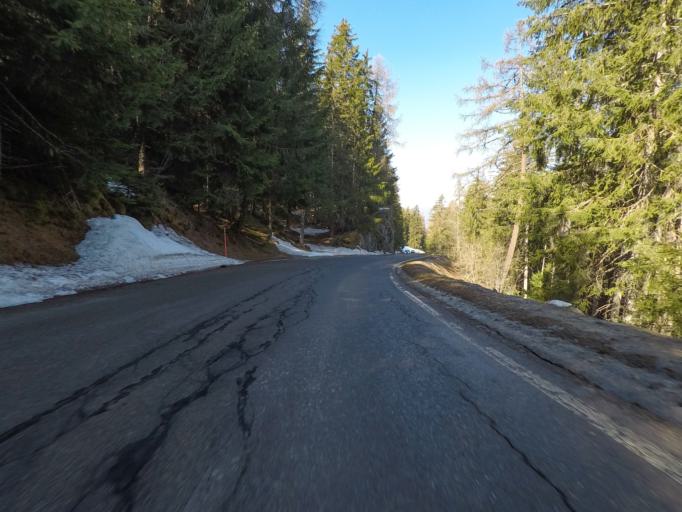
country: CH
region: Valais
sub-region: Herens District
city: Vex
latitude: 46.1993
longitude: 7.3753
